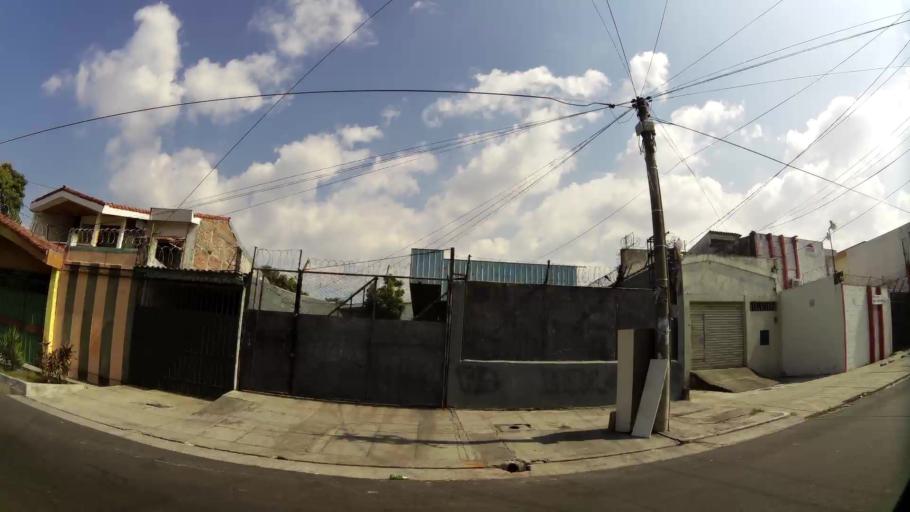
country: SV
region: San Salvador
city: Mejicanos
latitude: 13.7214
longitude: -89.2122
